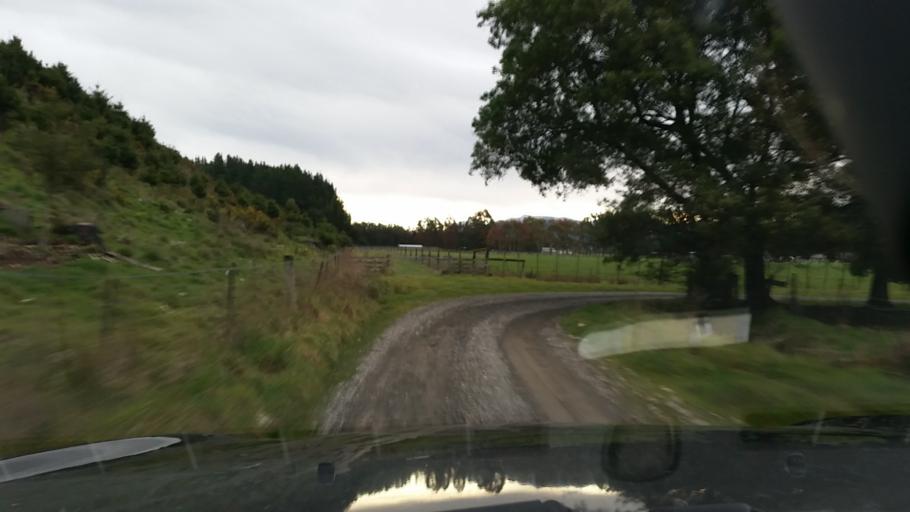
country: NZ
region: Marlborough
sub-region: Marlborough District
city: Blenheim
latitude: -41.5444
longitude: 173.6088
